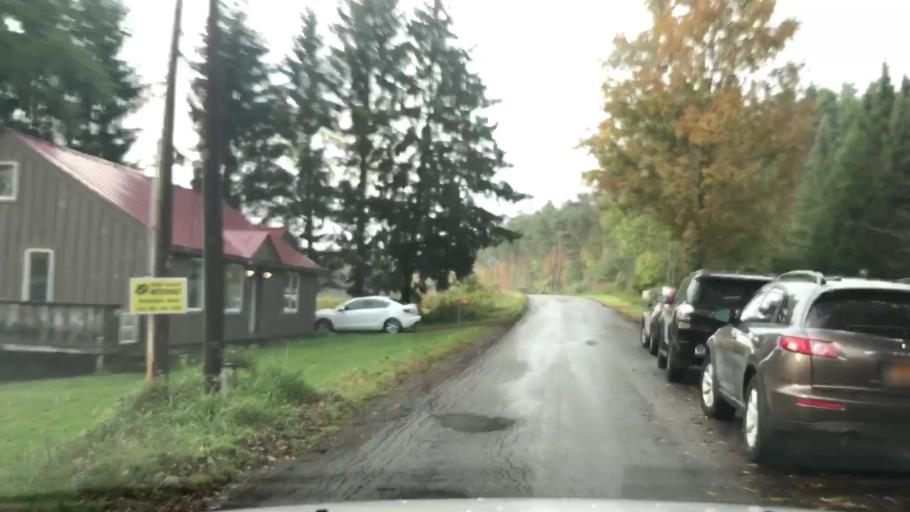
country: US
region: New York
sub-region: Cattaraugus County
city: Little Valley
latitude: 42.3054
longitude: -78.7162
